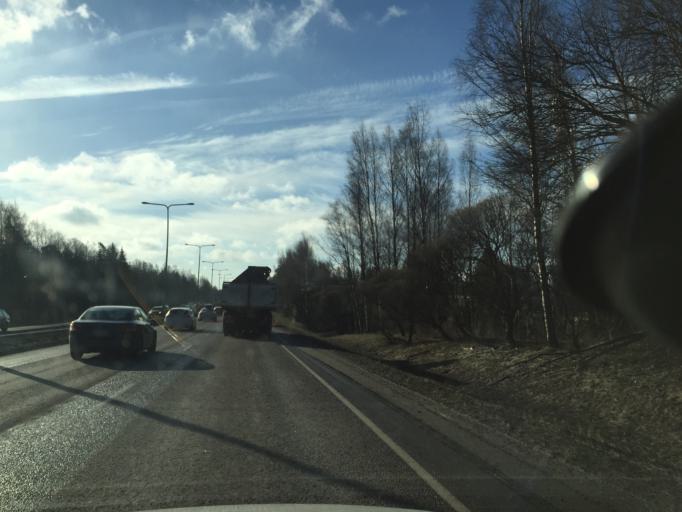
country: FI
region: Uusimaa
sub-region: Helsinki
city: Teekkarikylae
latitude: 60.2501
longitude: 24.8859
